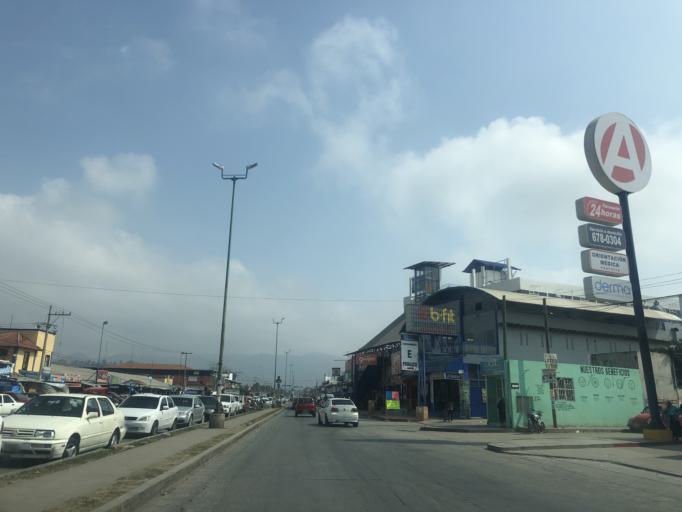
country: MX
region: Chiapas
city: San Cristobal de las Casas
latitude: 16.7188
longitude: -92.6369
